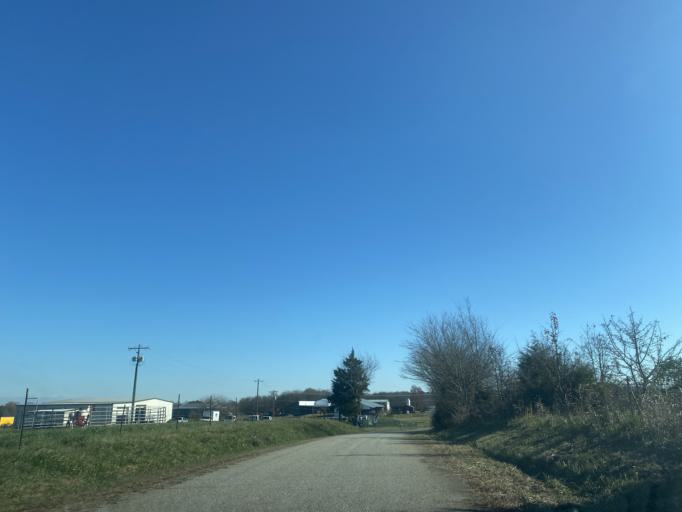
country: US
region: South Carolina
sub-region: Spartanburg County
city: Mayo
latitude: 35.1326
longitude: -81.7922
